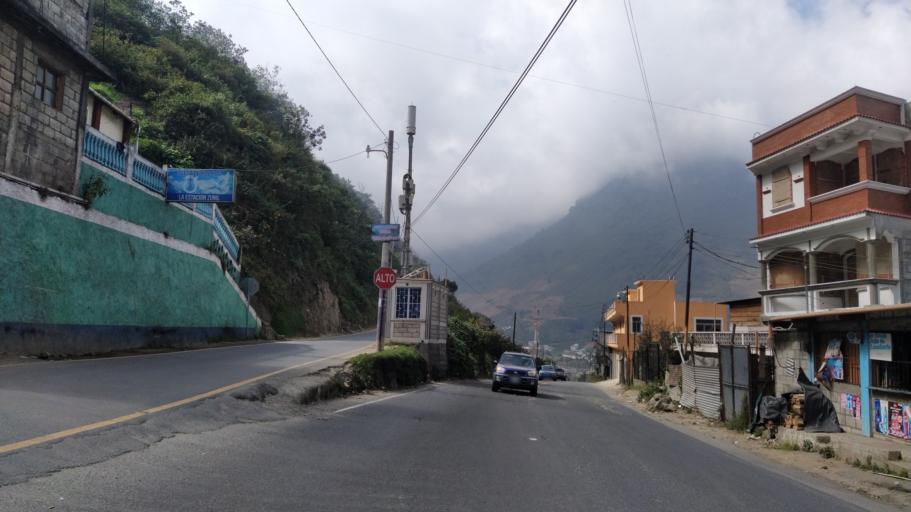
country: GT
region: Quetzaltenango
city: Zunil
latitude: 14.7816
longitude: -91.4844
